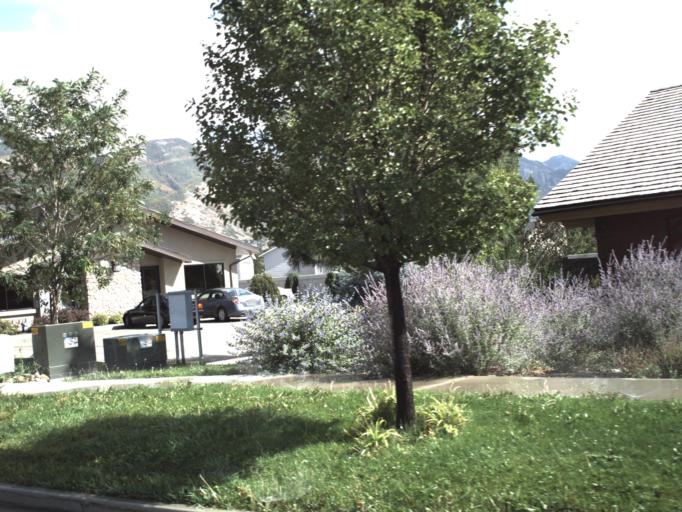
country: US
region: Utah
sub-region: Utah County
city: Orem
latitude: 40.3119
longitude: -111.6737
